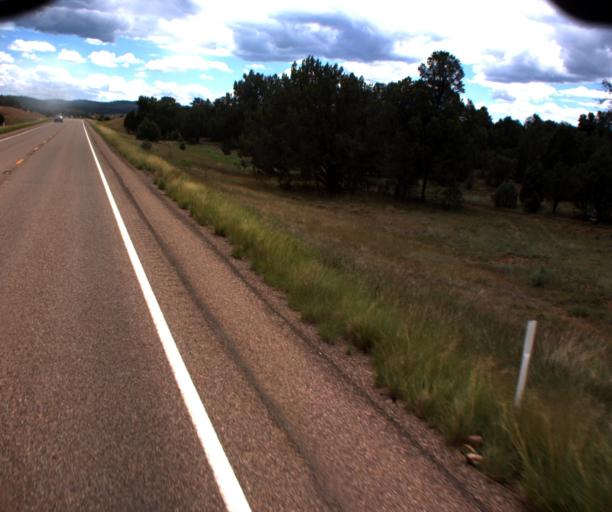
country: US
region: Arizona
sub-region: Navajo County
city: Linden
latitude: 34.3214
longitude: -110.2521
